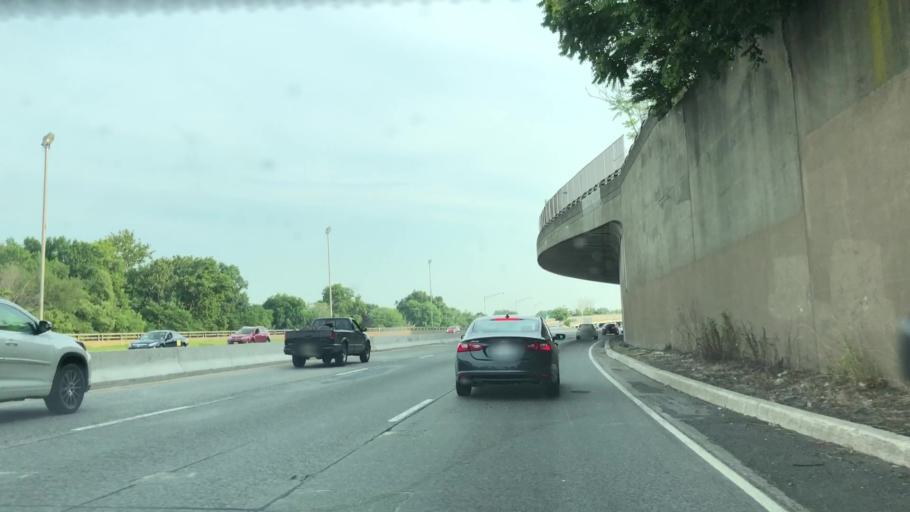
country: US
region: New Jersey
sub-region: Bergen County
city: Rutherford
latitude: 40.8296
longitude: -74.1220
